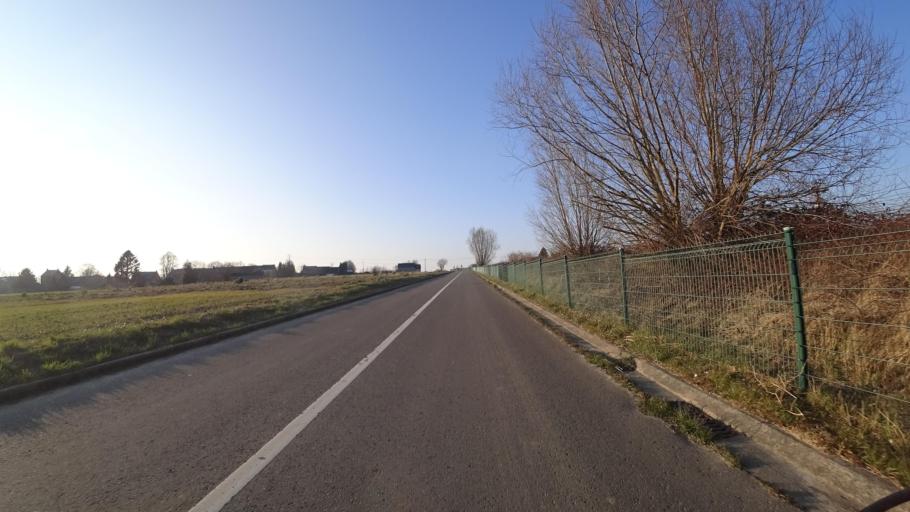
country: BE
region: Wallonia
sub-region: Province de Namur
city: Gembloux
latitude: 50.5762
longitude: 4.6849
